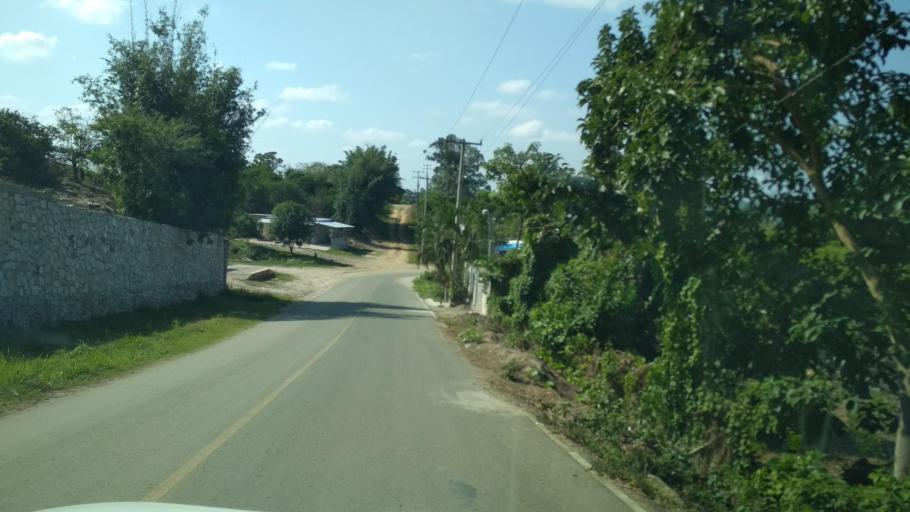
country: MX
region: Puebla
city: San Jose Acateno
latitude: 20.1907
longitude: -97.1536
